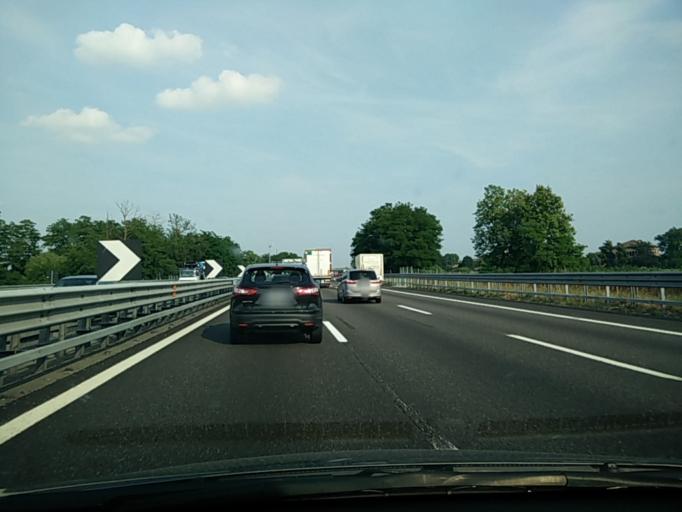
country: IT
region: Lombardy
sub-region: Citta metropolitana di Milano
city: Buccinasco
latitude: 45.4109
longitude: 9.1056
